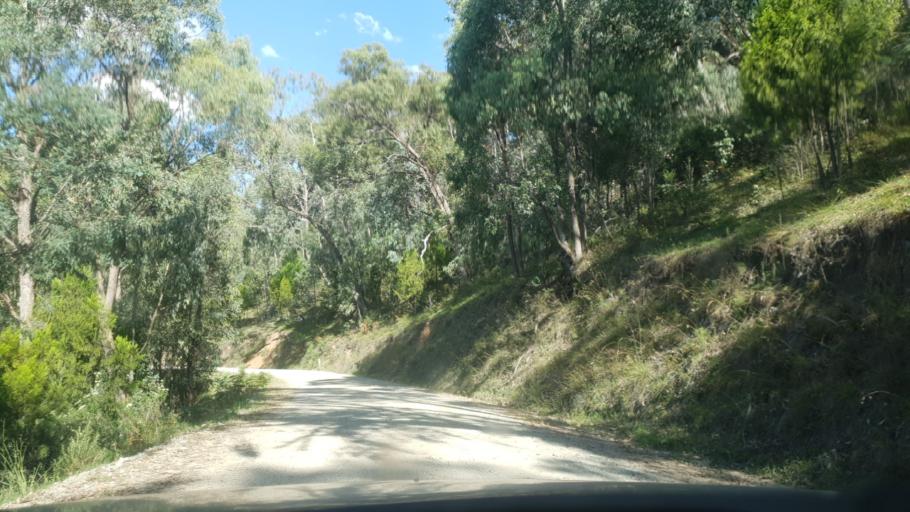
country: AU
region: Victoria
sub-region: Alpine
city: Mount Beauty
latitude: -36.7478
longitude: 147.1812
